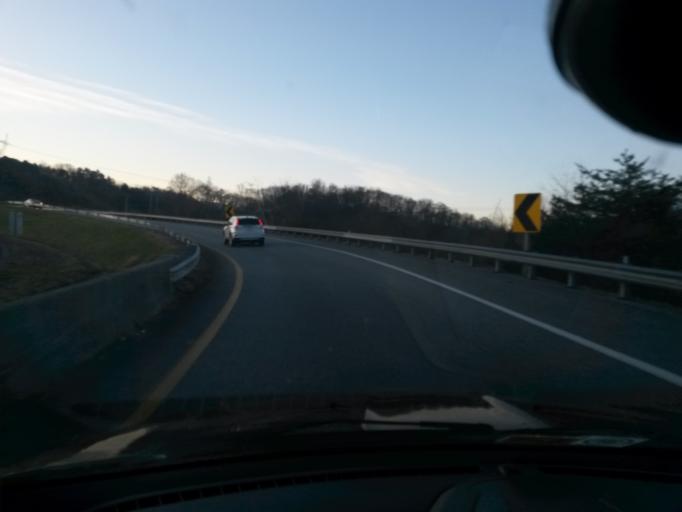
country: US
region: Virginia
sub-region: Botetourt County
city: Cloverdale
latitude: 37.3871
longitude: -79.9078
